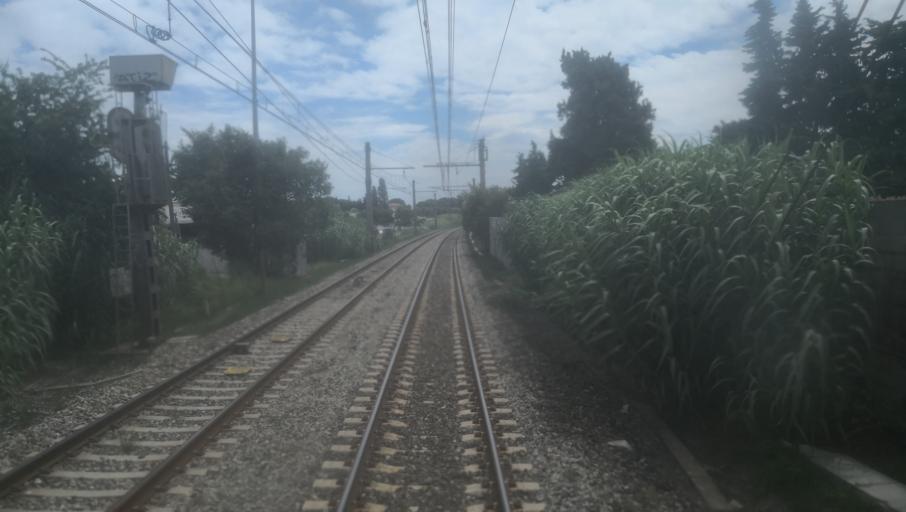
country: FR
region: Languedoc-Roussillon
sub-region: Departement de l'Herault
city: Montpellier
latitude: 43.5848
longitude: 3.8761
